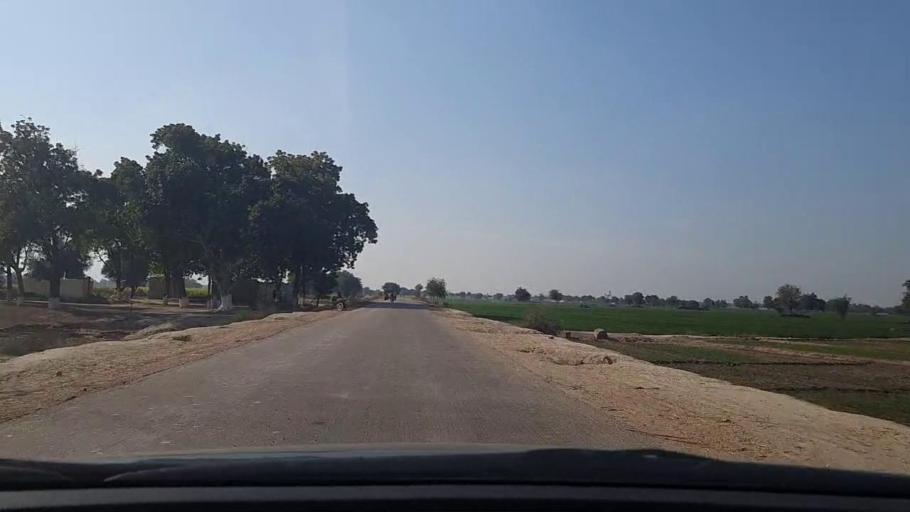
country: PK
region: Sindh
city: Daulatpur
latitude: 26.3180
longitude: 68.0558
